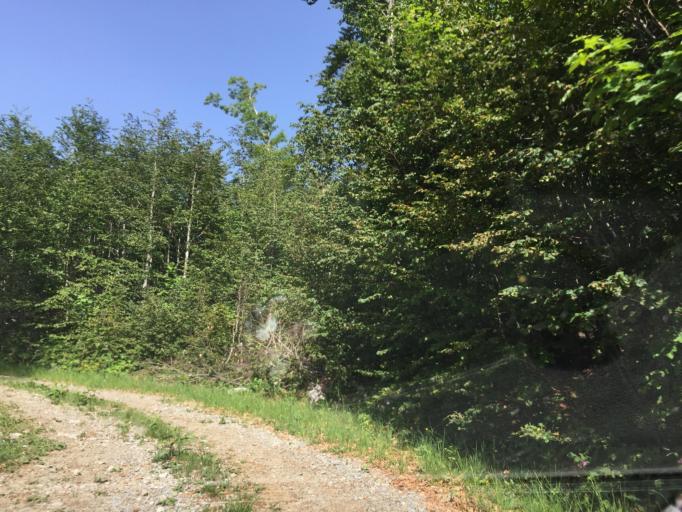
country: HR
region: Primorsko-Goranska
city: Podhum
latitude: 45.4264
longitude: 14.5830
